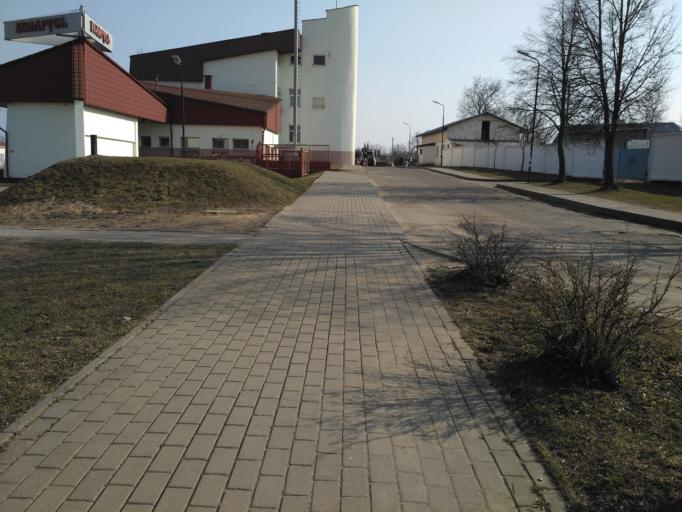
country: BY
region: Minsk
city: Zaslawye
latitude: 54.0094
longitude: 27.2830
